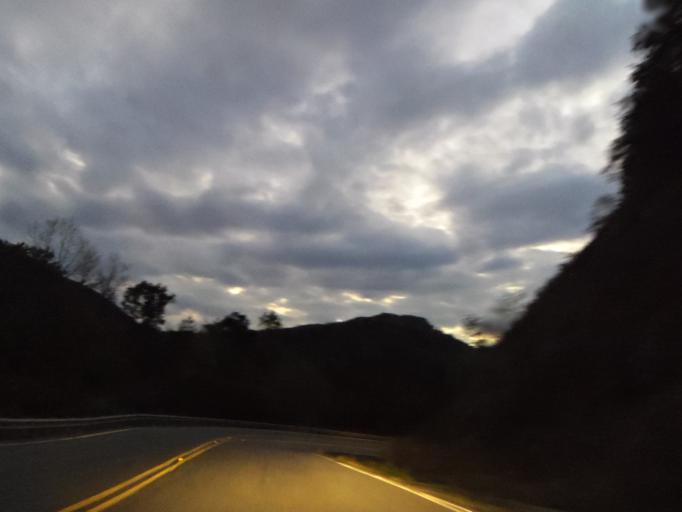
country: US
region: North Carolina
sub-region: Madison County
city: Marshall
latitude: 35.9108
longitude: -82.7525
